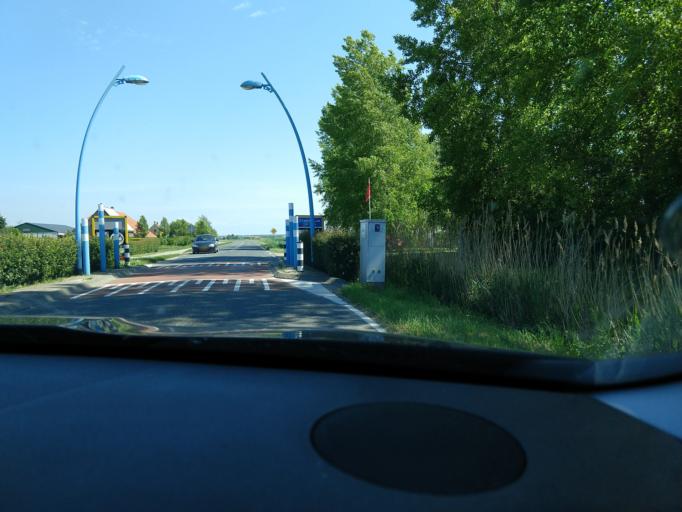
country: NL
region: Zeeland
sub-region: Gemeente Reimerswaal
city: Yerseke
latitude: 51.5839
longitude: 4.0191
